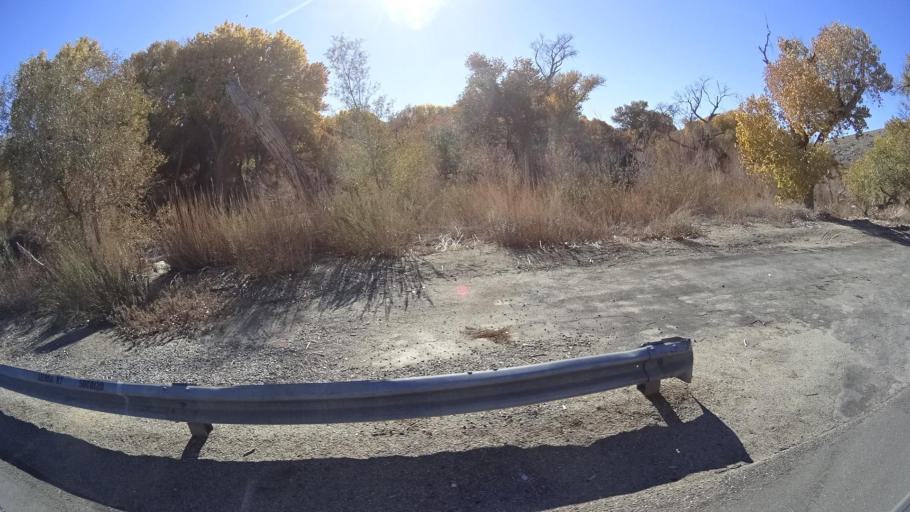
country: US
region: California
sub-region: Kern County
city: Weldon
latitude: 35.6726
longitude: -118.3276
